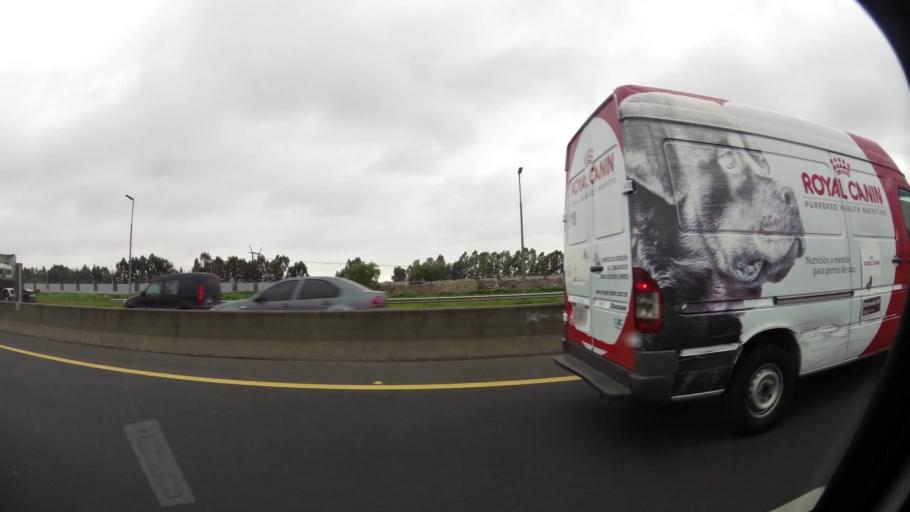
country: AR
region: Buenos Aires
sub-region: Partido de Quilmes
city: Quilmes
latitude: -34.7525
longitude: -58.1923
